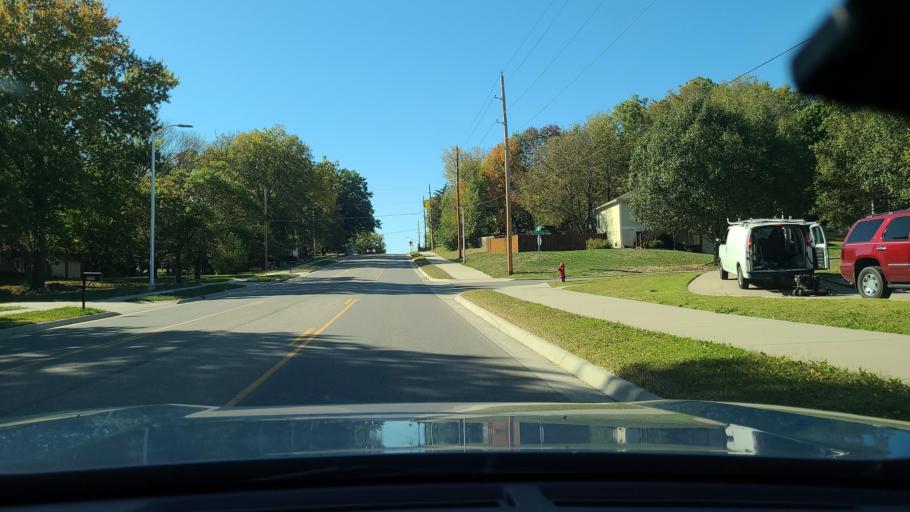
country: US
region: Kansas
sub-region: Shawnee County
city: Topeka
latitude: 39.0005
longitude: -95.7183
